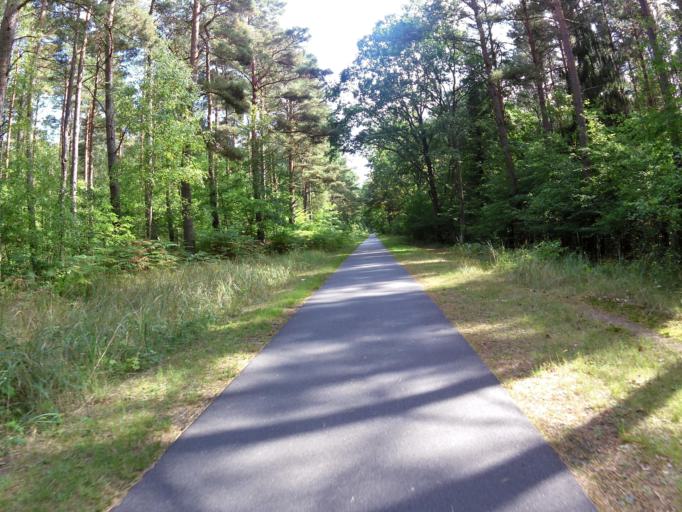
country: DE
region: Mecklenburg-Vorpommern
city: Karlshagen
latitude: 54.1284
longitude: 13.8196
